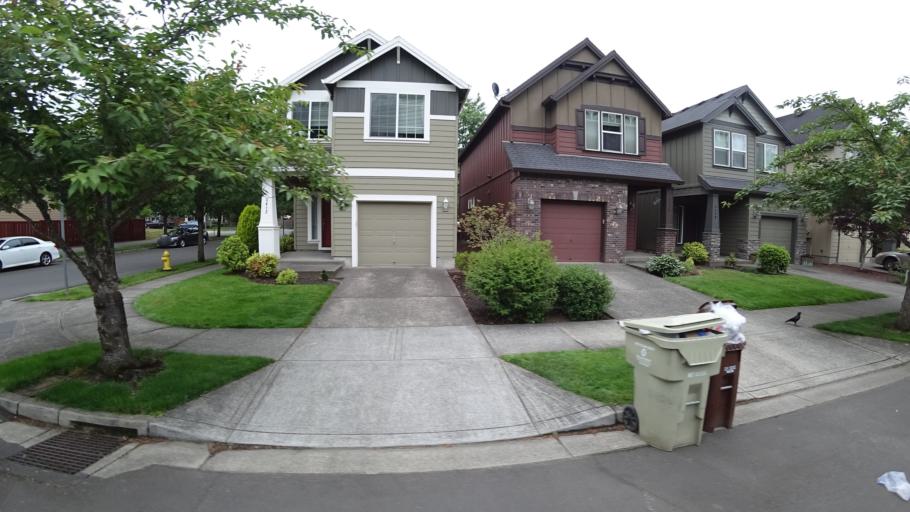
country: US
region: Oregon
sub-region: Washington County
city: Hillsboro
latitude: 45.4952
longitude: -122.9373
